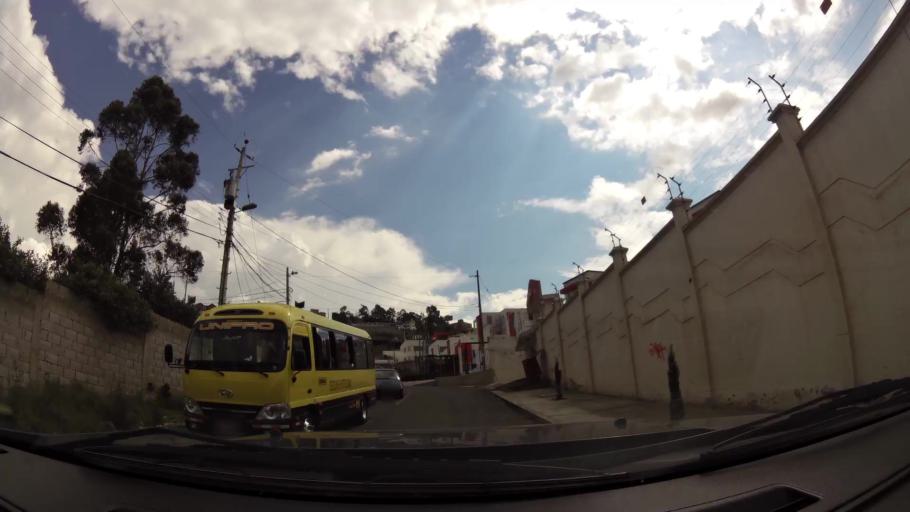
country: EC
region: Pichincha
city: Quito
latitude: -0.0967
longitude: -78.4619
